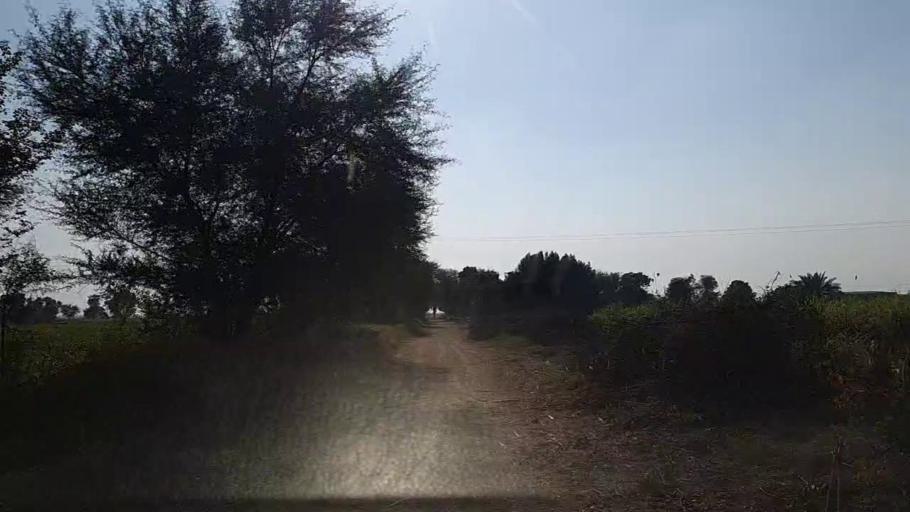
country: PK
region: Sindh
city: Daur
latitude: 26.3843
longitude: 68.3247
